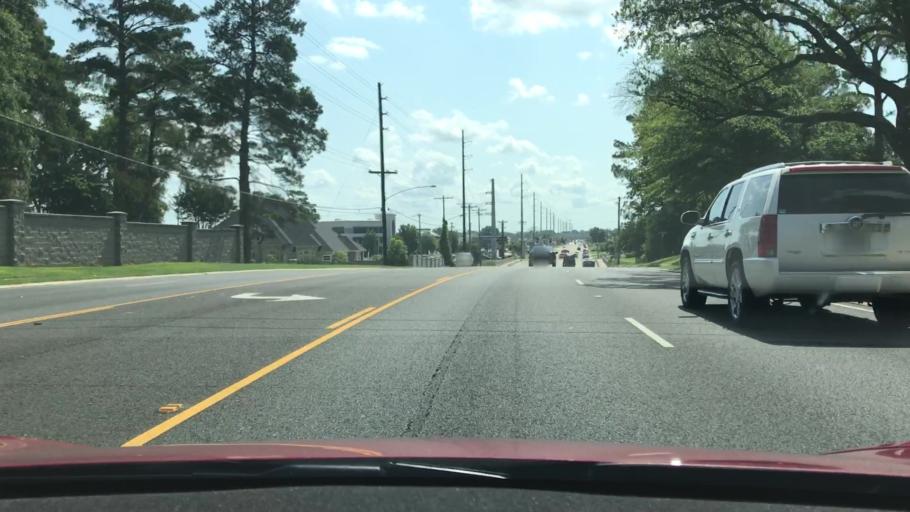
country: US
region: Louisiana
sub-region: Bossier Parish
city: Bossier City
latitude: 32.4434
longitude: -93.7329
